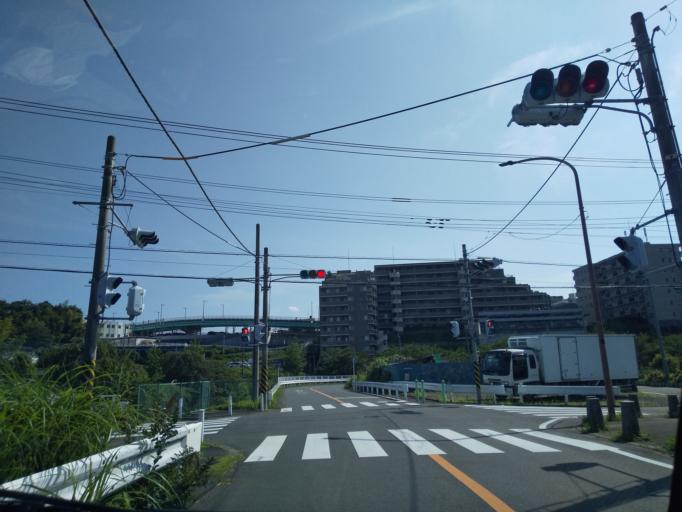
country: JP
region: Kanagawa
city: Zama
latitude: 35.4691
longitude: 139.4152
